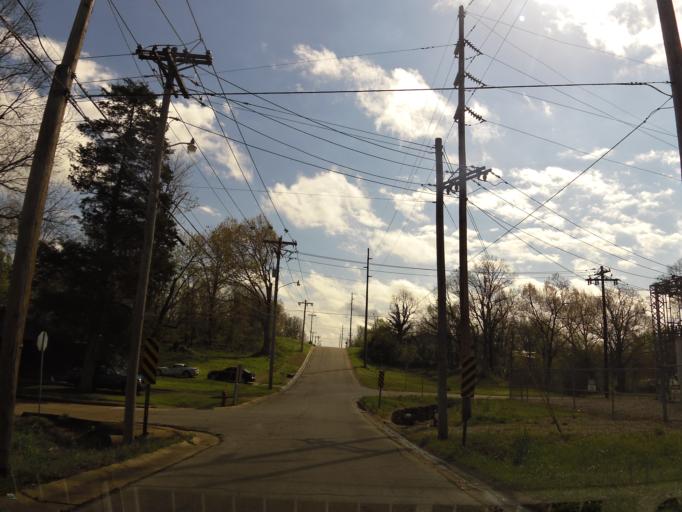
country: US
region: Missouri
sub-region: Butler County
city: Poplar Bluff
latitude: 36.7664
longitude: -90.3989
